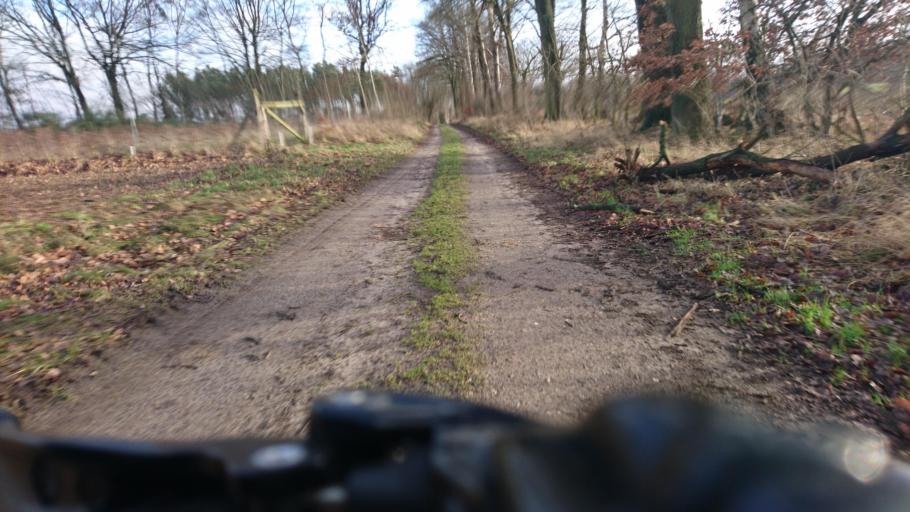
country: DE
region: Lower Saxony
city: Altenmedingen
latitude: 53.1685
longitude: 10.6247
